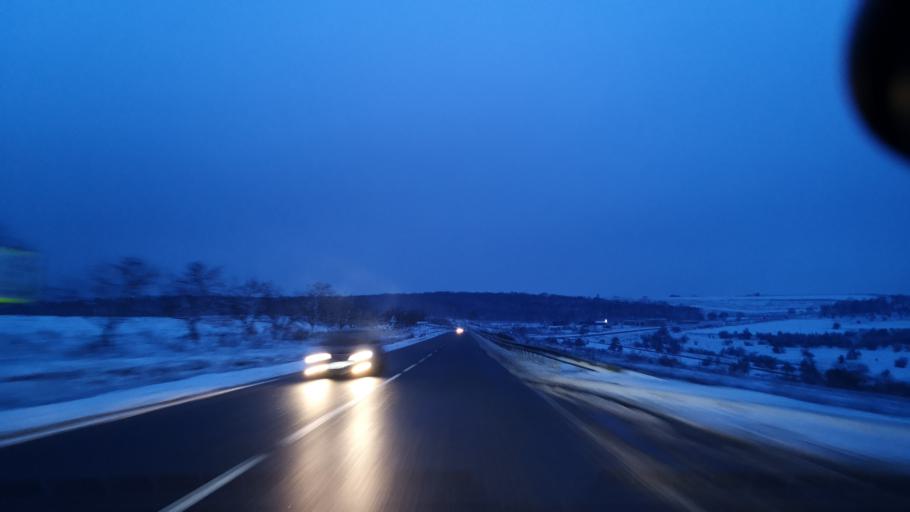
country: MD
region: Rezina
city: Saharna
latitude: 47.6046
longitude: 28.8311
